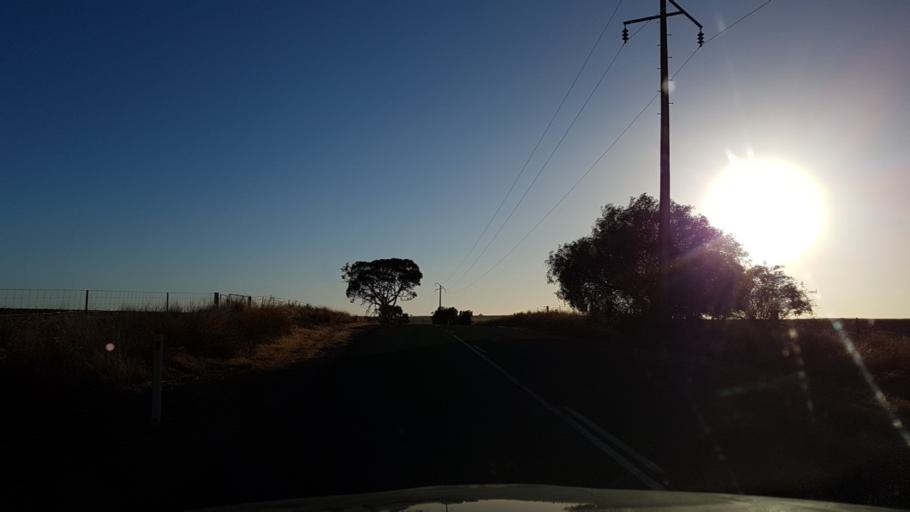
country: AU
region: South Australia
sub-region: Clare and Gilbert Valleys
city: Clare
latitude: -34.0189
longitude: 138.7099
